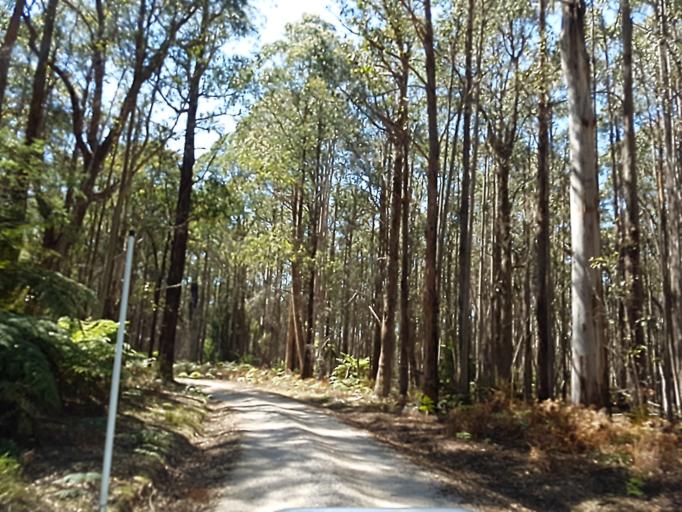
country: AU
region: Victoria
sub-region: East Gippsland
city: Lakes Entrance
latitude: -37.2914
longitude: 148.3187
